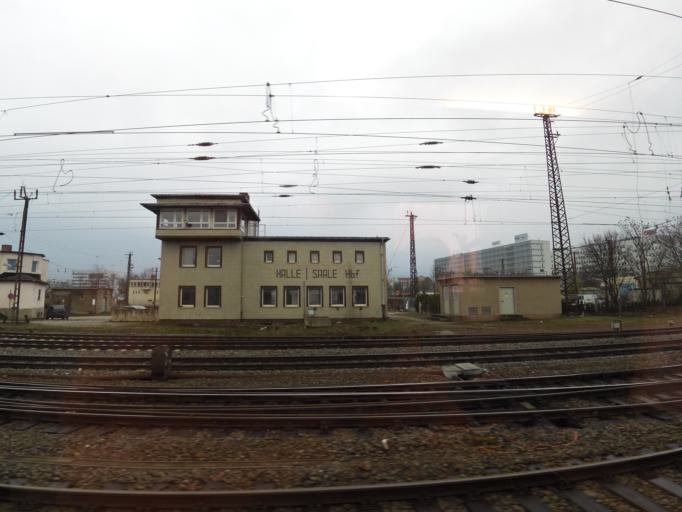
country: DE
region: Saxony-Anhalt
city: Halle (Saale)
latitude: 51.4809
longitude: 11.9864
